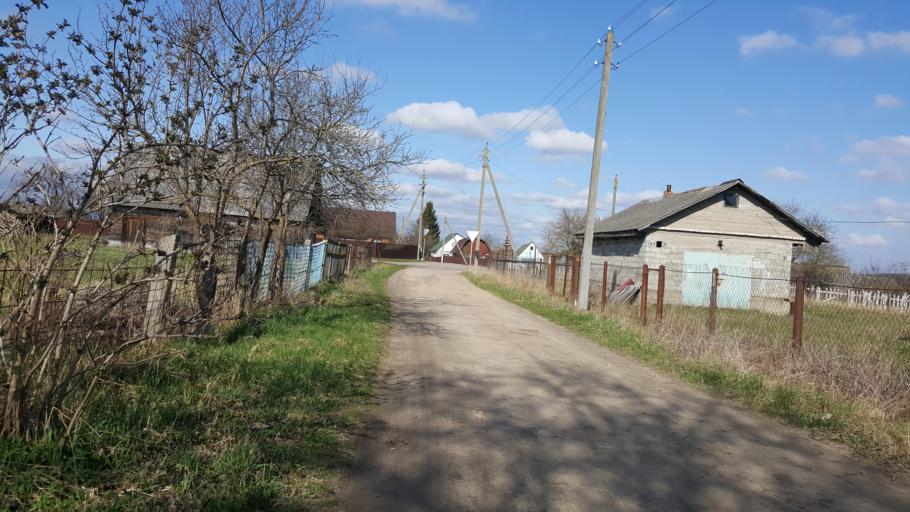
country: BY
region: Brest
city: Kamyanyets
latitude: 52.4061
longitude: 23.7962
